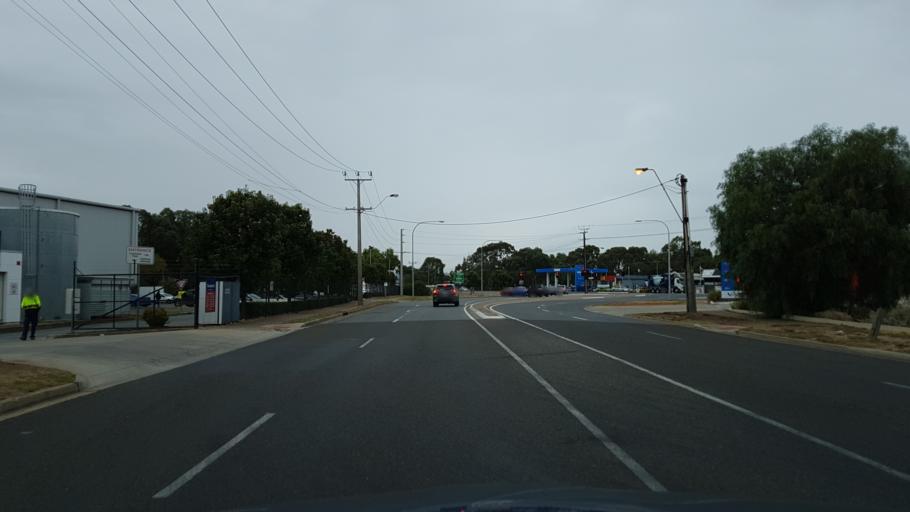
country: AU
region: South Australia
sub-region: Salisbury
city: Ingle Farm
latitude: -34.8262
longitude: 138.6147
